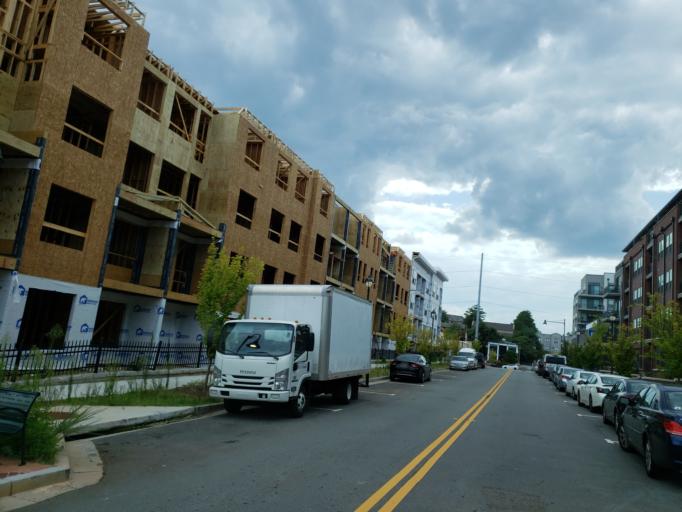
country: US
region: Georgia
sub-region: Fulton County
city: Sandy Springs
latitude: 33.9216
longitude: -84.3773
